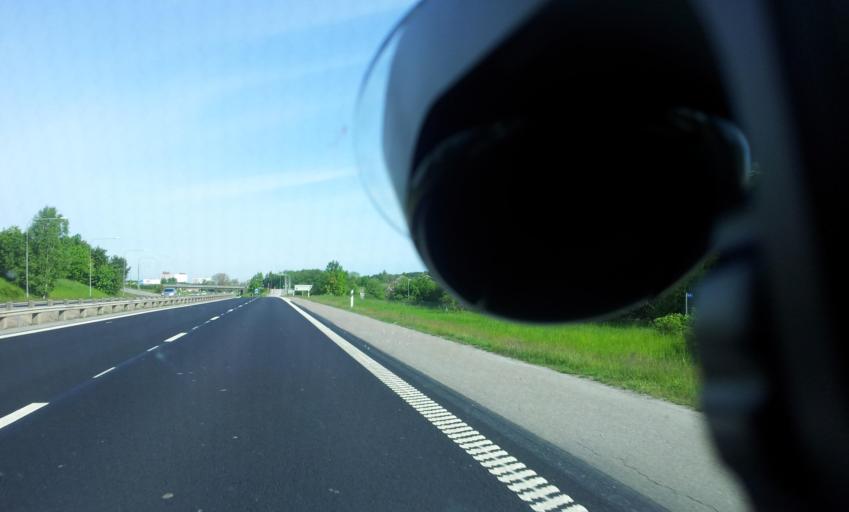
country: SE
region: OEstergoetland
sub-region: Norrkopings Kommun
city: Norrkoping
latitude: 58.5619
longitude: 16.2247
